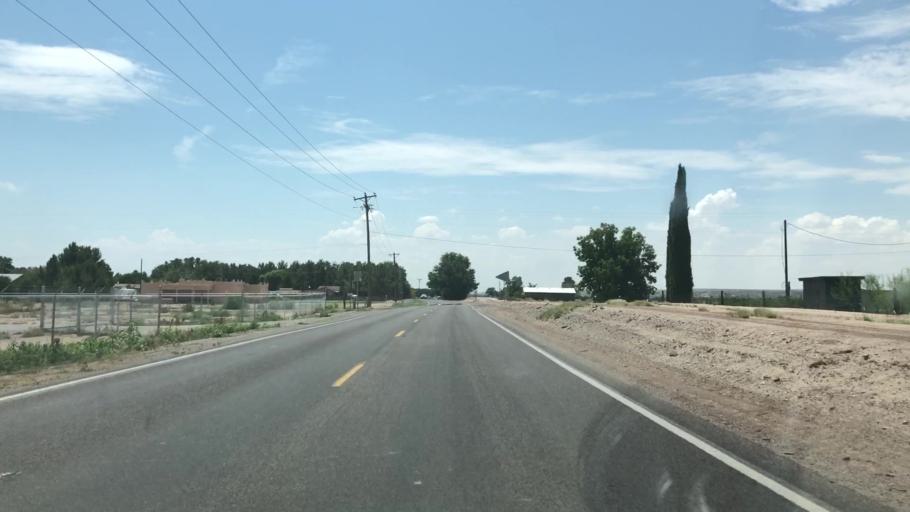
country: US
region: New Mexico
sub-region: Dona Ana County
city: Vado
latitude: 32.0870
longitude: -106.6834
